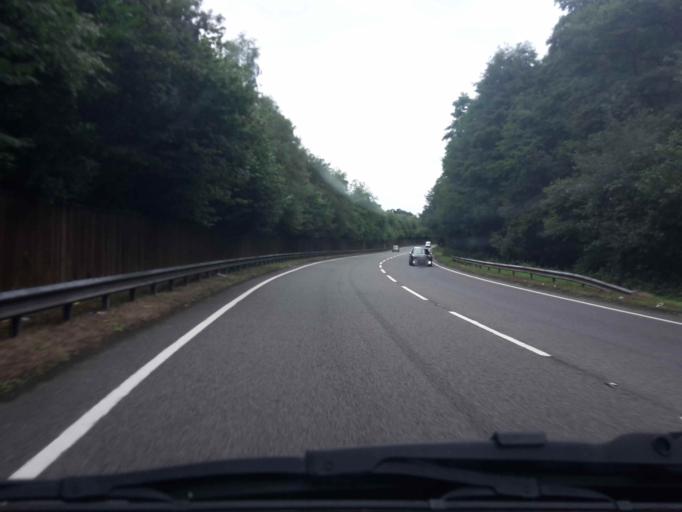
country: GB
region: England
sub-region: Hampshire
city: Fleet
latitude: 51.2979
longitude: -0.7965
